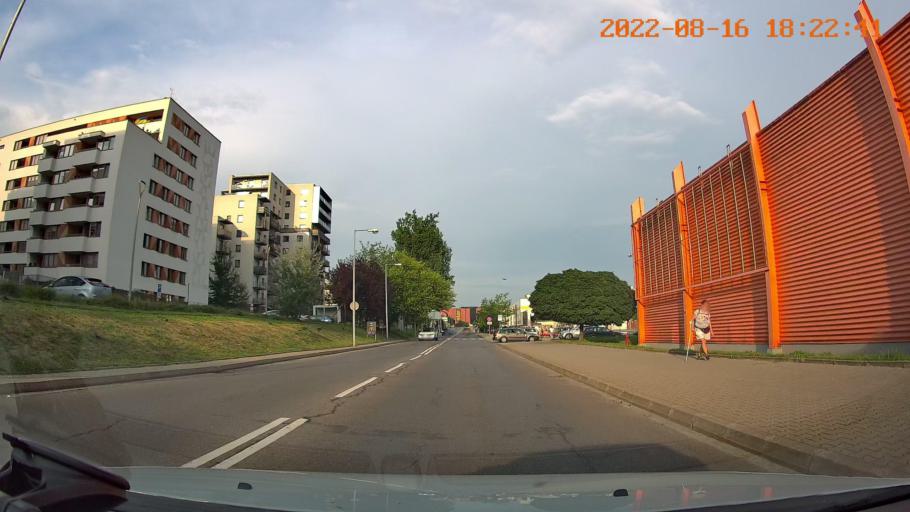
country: PL
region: Lesser Poland Voivodeship
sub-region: Krakow
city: Krakow
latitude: 50.0878
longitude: 19.9779
